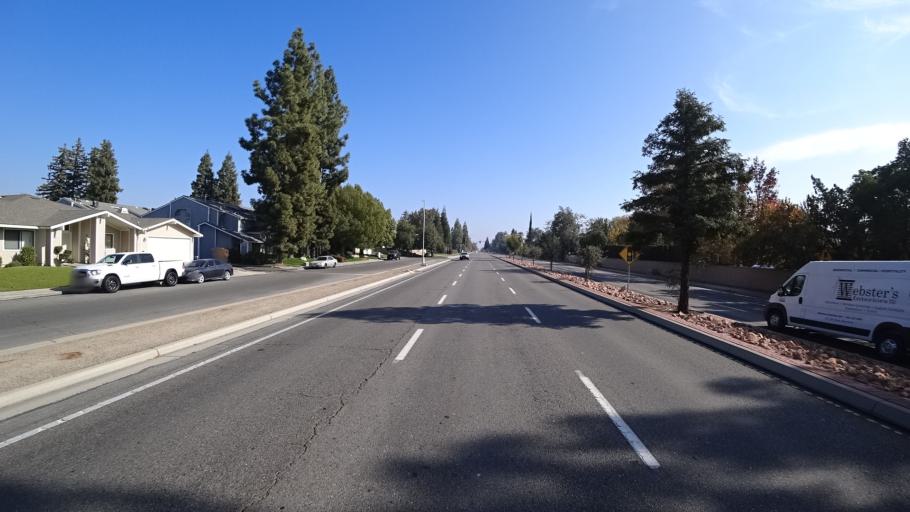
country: US
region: California
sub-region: Kern County
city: Greenacres
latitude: 35.3544
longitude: -119.0850
